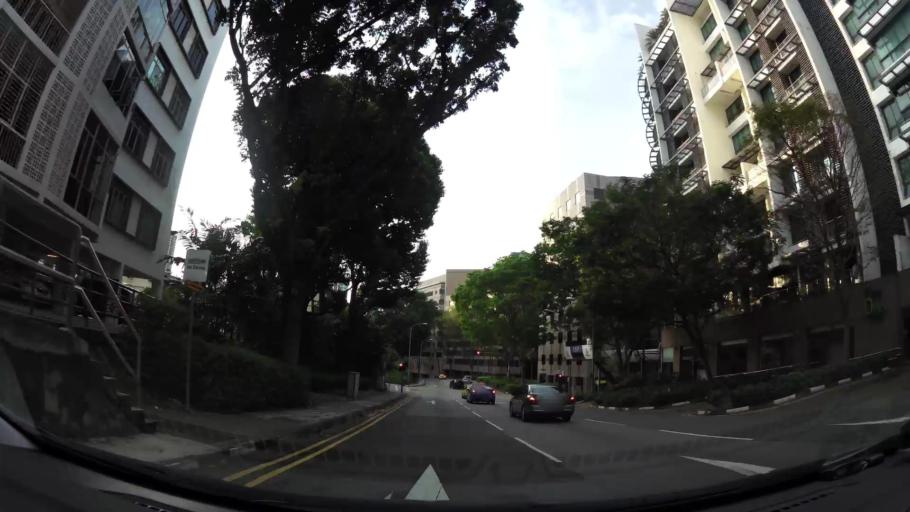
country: SG
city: Singapore
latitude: 1.2989
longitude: 103.8418
